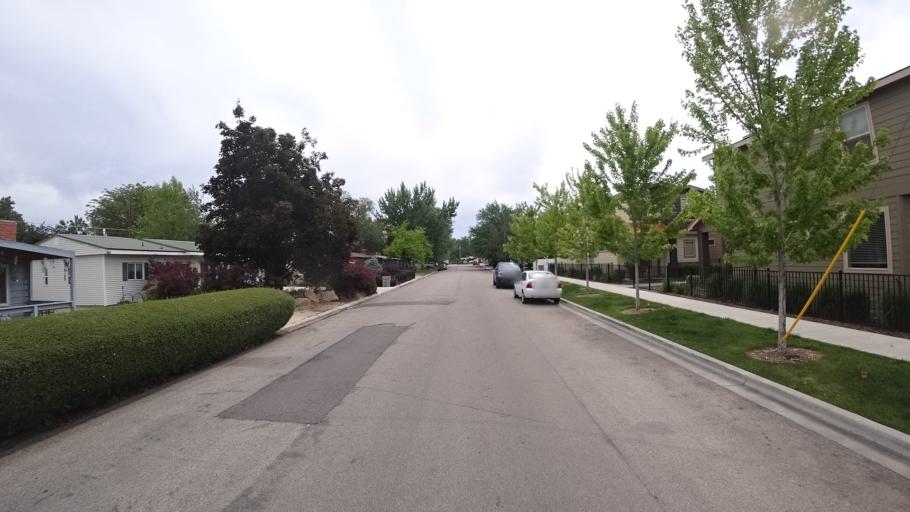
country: US
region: Idaho
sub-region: Ada County
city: Boise
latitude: 43.5790
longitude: -116.2155
